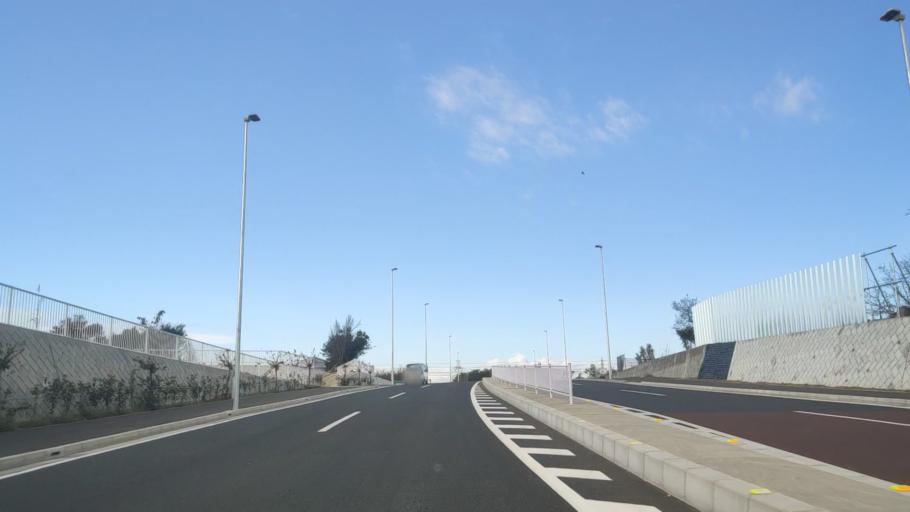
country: JP
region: Kanagawa
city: Minami-rinkan
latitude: 35.4259
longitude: 139.4901
